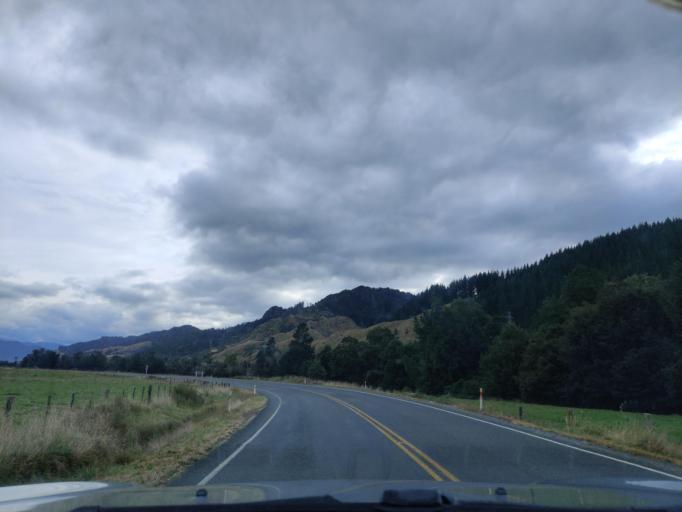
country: NZ
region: Tasman
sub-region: Tasman District
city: Wakefield
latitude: -41.7662
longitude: 172.3849
